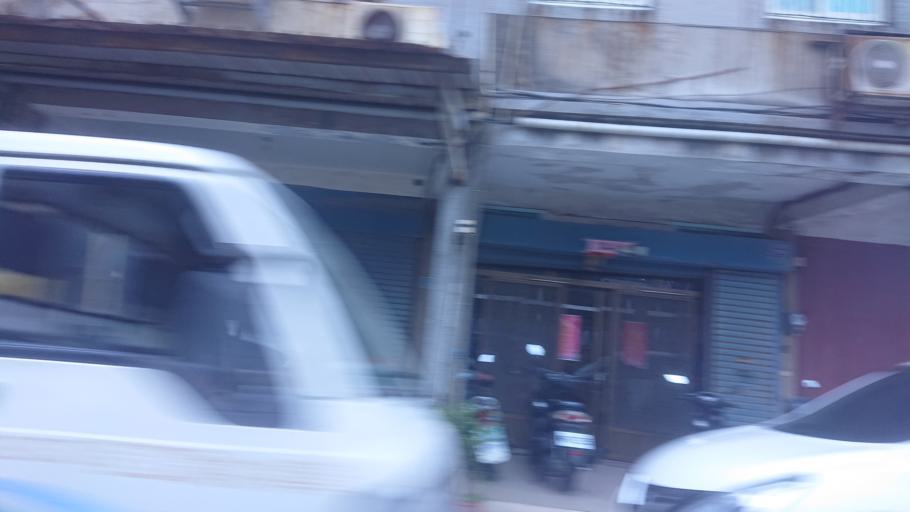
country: TW
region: Fukien
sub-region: Kinmen
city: Jincheng
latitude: 24.4341
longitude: 118.3139
